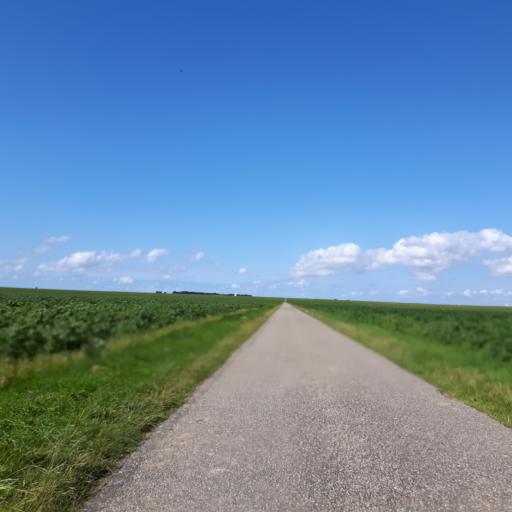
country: NL
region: Zeeland
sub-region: Gemeente Goes
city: Goes
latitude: 51.5375
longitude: 3.8839
